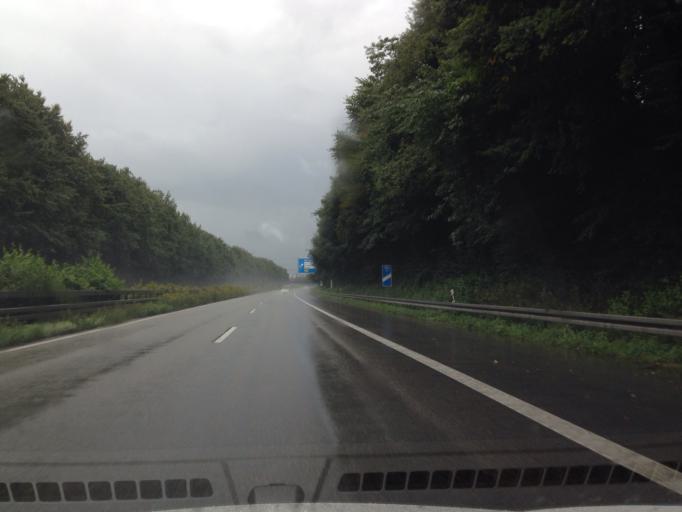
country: DE
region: North Rhine-Westphalia
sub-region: Regierungsbezirk Munster
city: Gladbeck
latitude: 51.6168
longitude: 7.0351
